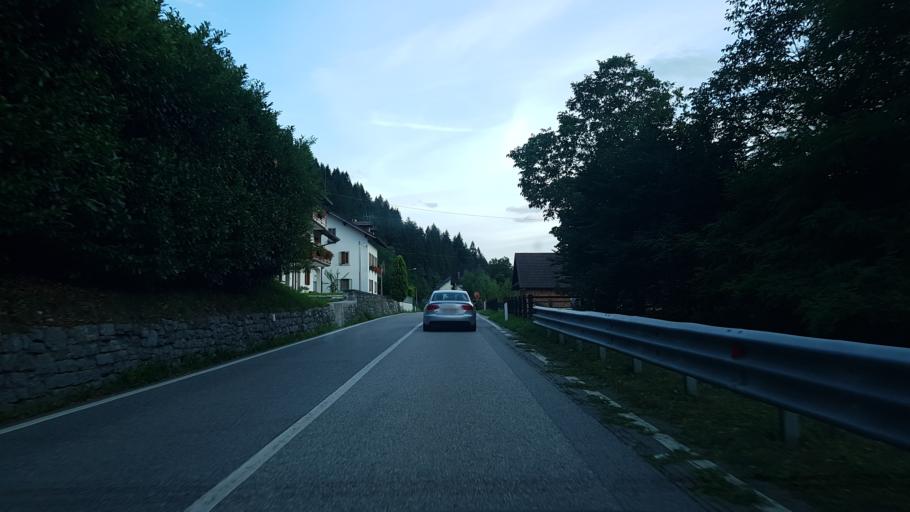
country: IT
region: Friuli Venezia Giulia
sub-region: Provincia di Udine
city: Ovaro
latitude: 46.4986
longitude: 12.8662
